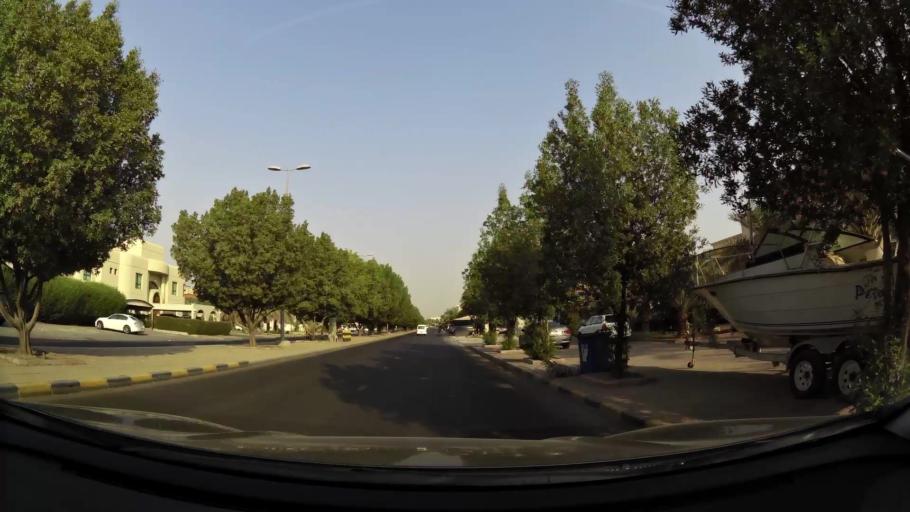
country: KW
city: Bayan
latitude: 29.3009
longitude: 48.0487
